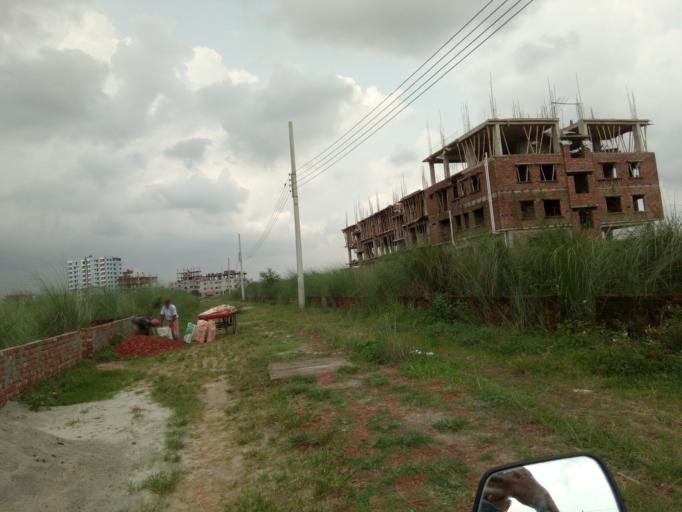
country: BD
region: Dhaka
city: Azimpur
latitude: 23.7504
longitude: 90.3494
